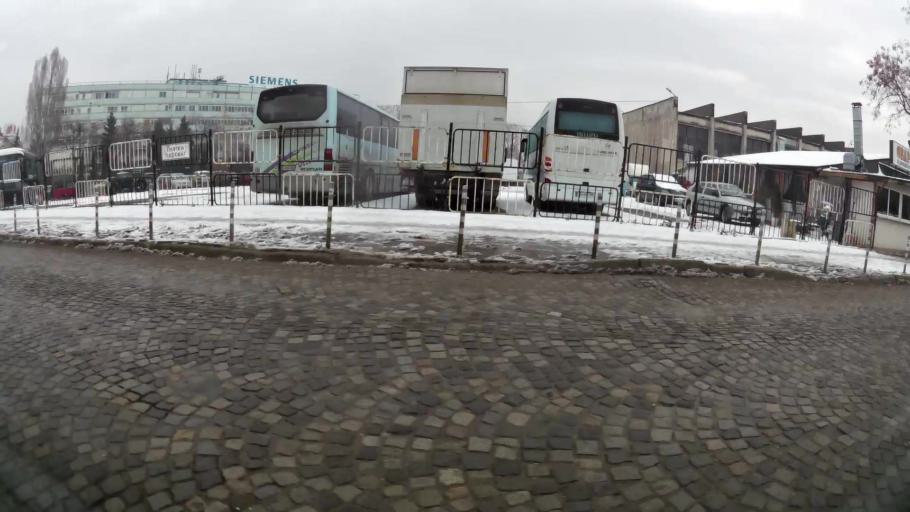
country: BG
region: Sofia-Capital
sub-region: Stolichna Obshtina
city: Sofia
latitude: 42.7158
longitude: 23.2972
